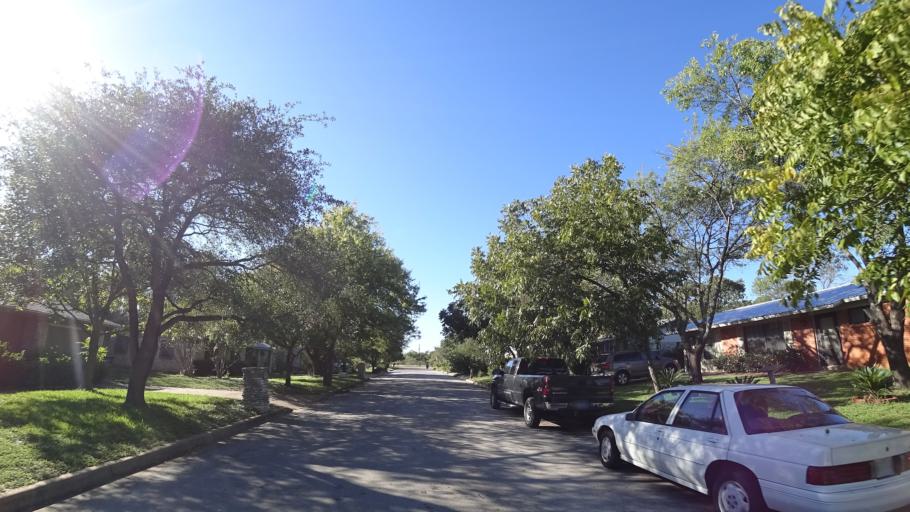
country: US
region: Texas
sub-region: Travis County
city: Rollingwood
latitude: 30.2346
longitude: -97.8093
